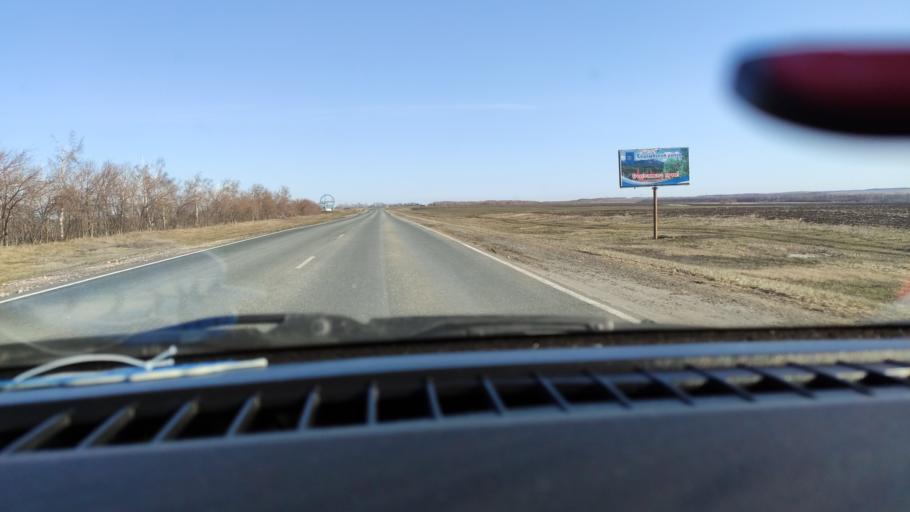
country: RU
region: Saratov
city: Dukhovnitskoye
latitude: 52.8000
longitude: 48.2302
